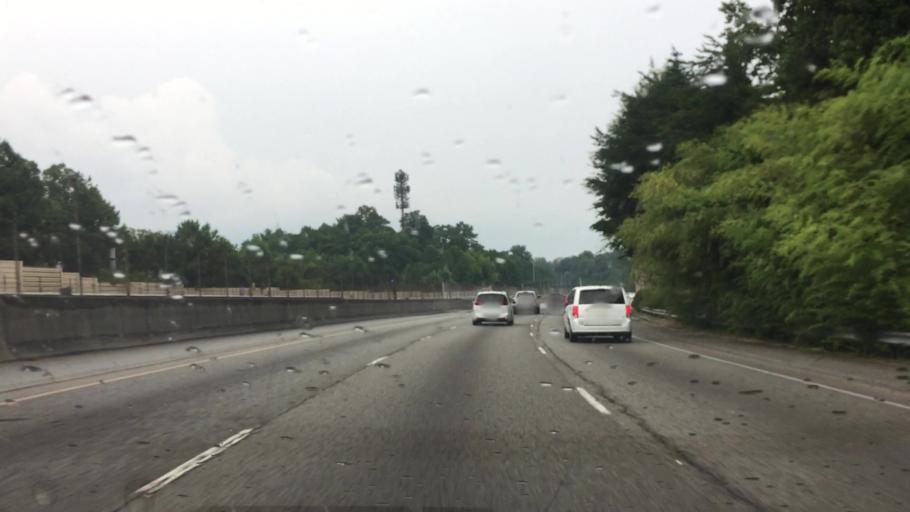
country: US
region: Georgia
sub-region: DeKalb County
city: North Atlanta
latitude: 33.8706
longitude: -84.3655
